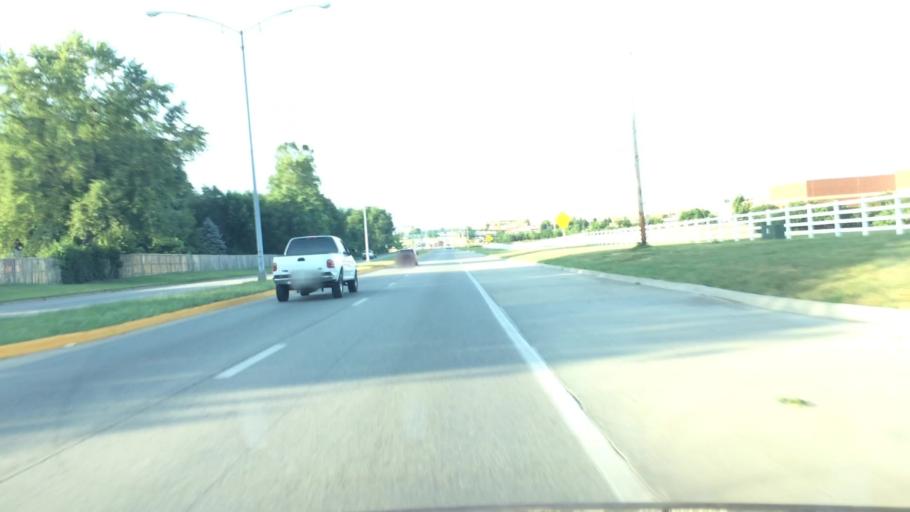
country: US
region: Missouri
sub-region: Greene County
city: Springfield
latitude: 37.1715
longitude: -93.3161
